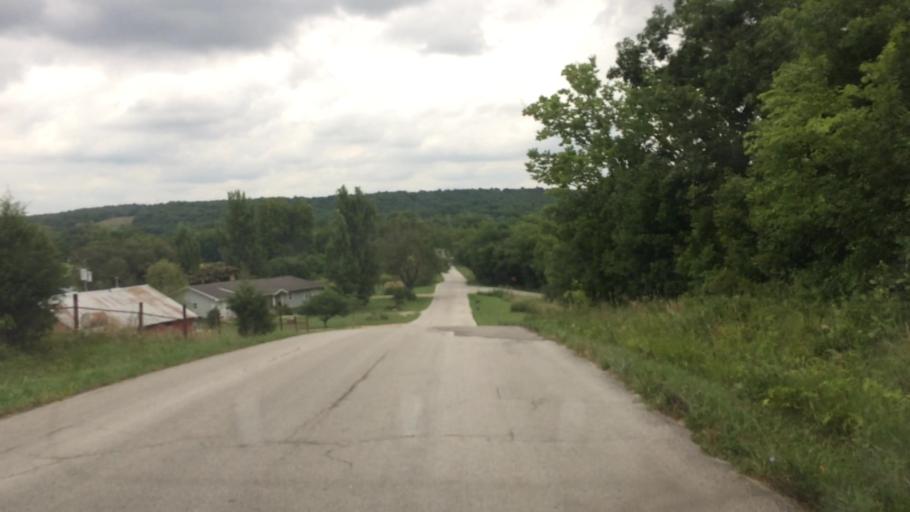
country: US
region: Missouri
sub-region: Greene County
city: Strafford
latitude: 37.3222
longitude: -93.0577
